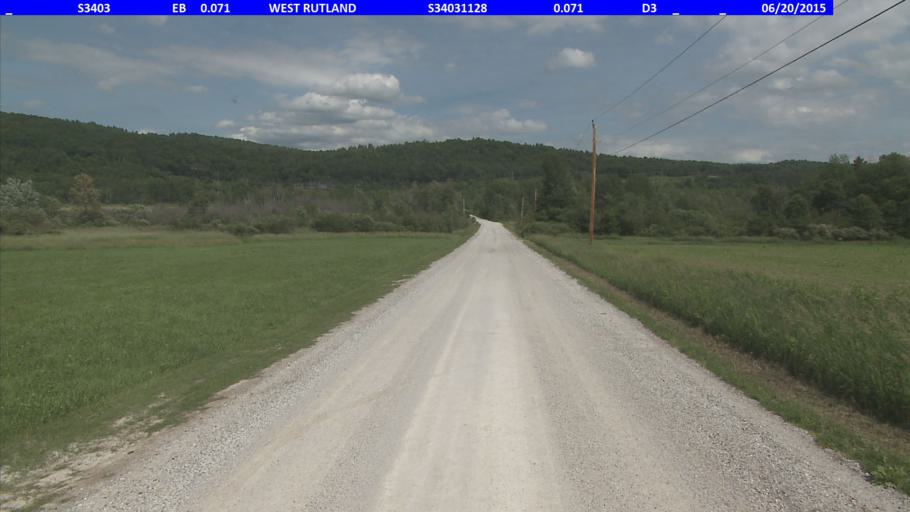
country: US
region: Vermont
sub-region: Rutland County
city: West Rutland
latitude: 43.6311
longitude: -73.0668
